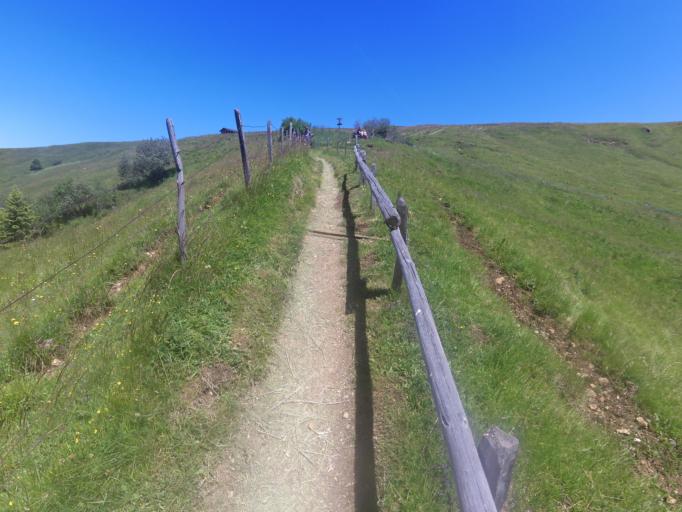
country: IT
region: Trentino-Alto Adige
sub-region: Bolzano
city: Siusi
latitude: 46.5242
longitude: 11.6063
